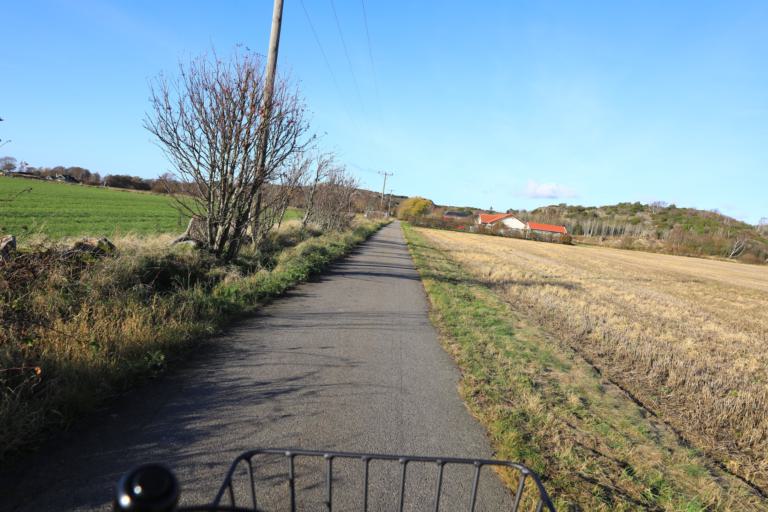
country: SE
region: Halland
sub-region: Varbergs Kommun
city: Varberg
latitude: 57.1521
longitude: 12.2438
